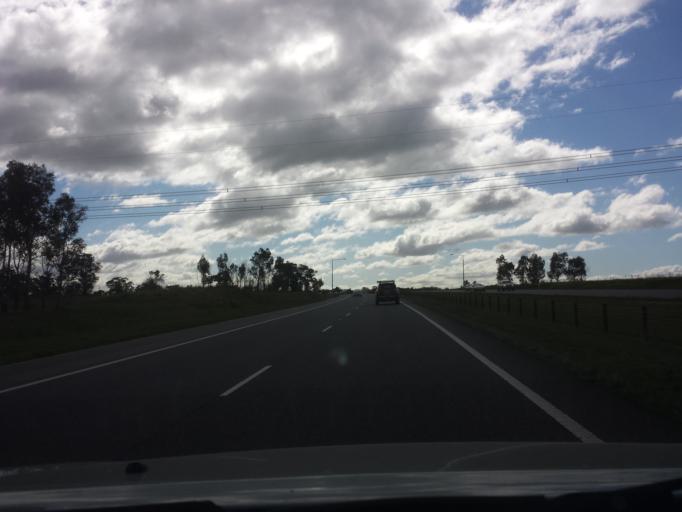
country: AU
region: Victoria
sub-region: Whittlesea
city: Lalor
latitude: -37.6307
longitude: 144.9939
